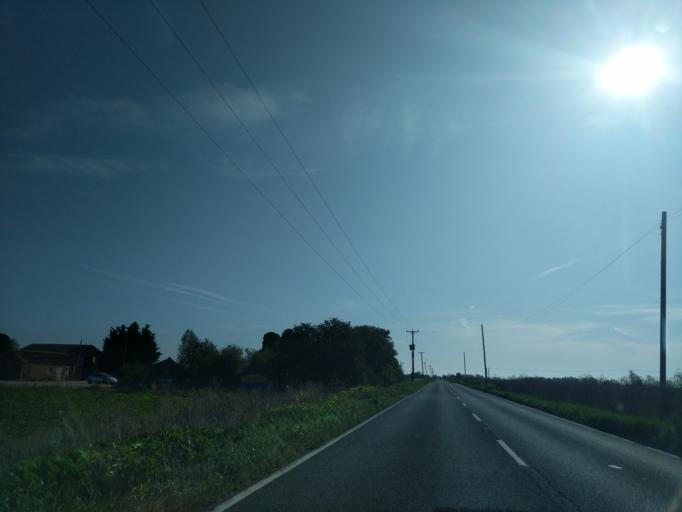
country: GB
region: England
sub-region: Lincolnshire
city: Bourne
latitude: 52.7722
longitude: -0.3314
